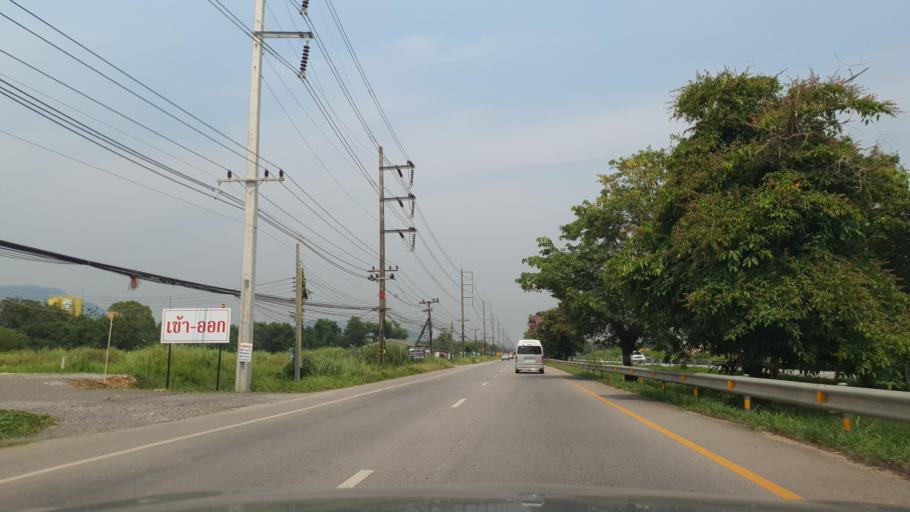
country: TH
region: Rayong
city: Rayong
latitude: 12.6390
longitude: 101.3723
